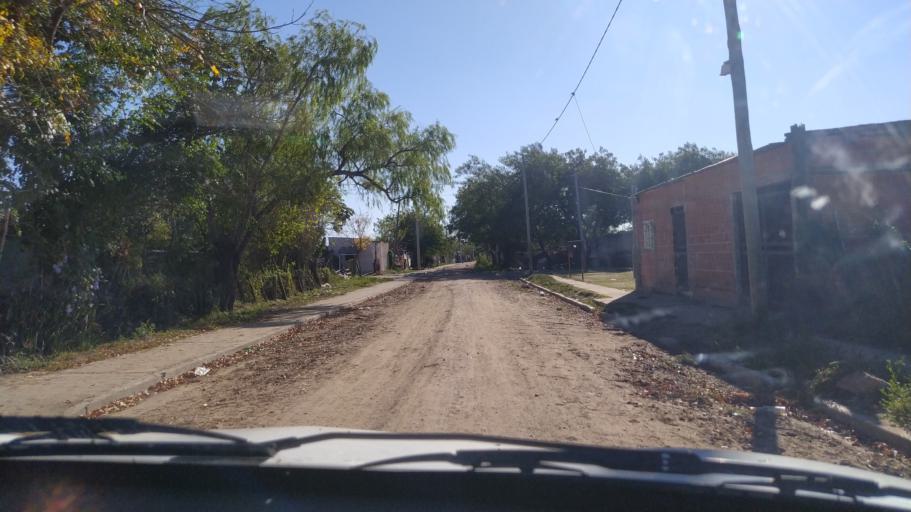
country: AR
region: Corrientes
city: Corrientes
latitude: -27.4976
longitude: -58.8046
